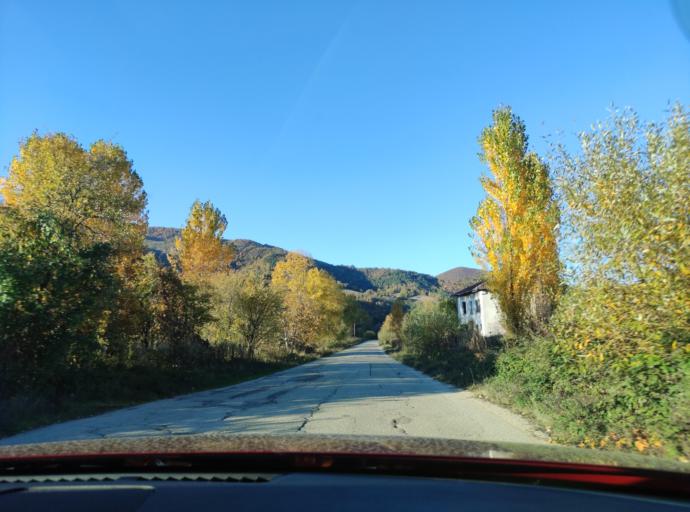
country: BG
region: Montana
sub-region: Obshtina Chiprovtsi
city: Chiprovtsi
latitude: 43.3878
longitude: 22.9223
